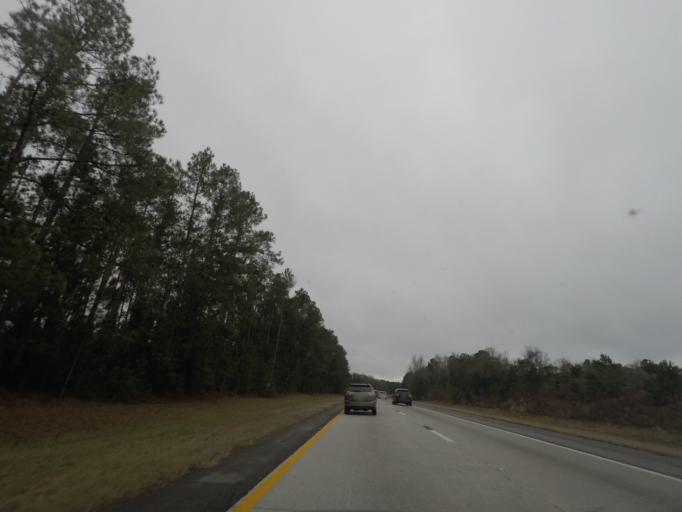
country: US
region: South Carolina
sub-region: Dorchester County
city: Saint George
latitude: 33.1502
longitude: -80.6244
